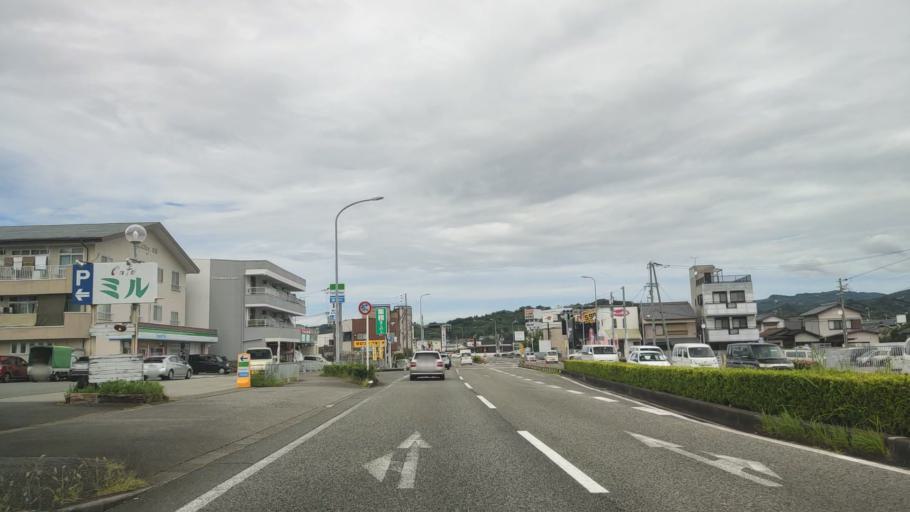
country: JP
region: Wakayama
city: Tanabe
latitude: 33.7389
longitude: 135.3945
